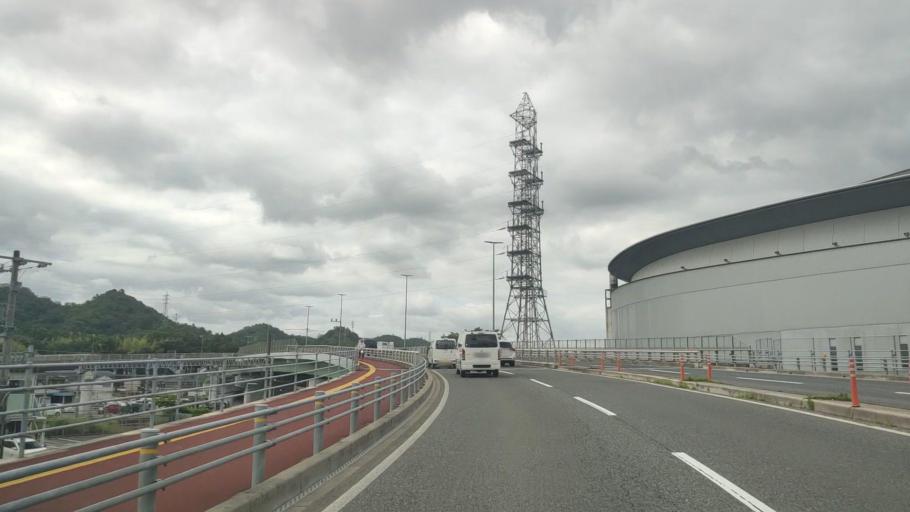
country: JP
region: Tottori
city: Yonago
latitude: 35.4213
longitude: 133.3341
